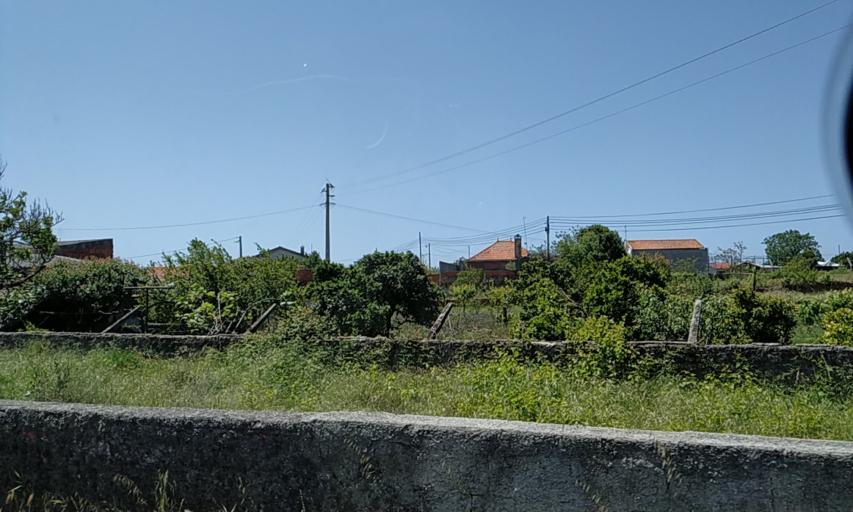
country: PT
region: Aveiro
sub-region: Aveiro
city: Aveiro
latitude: 40.6438
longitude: -8.6195
